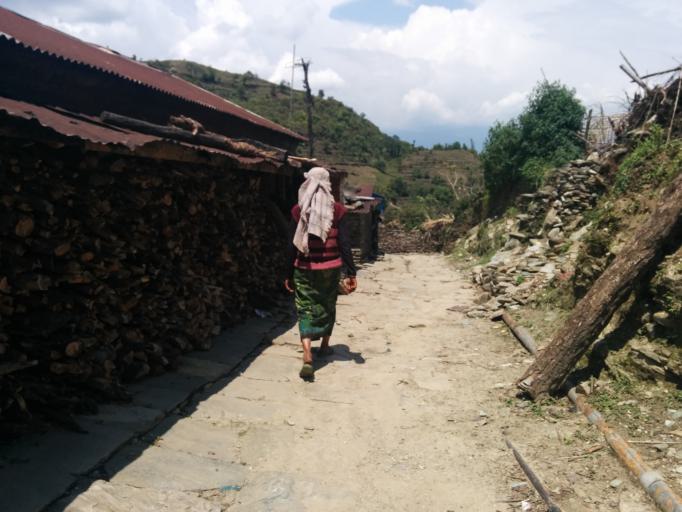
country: NP
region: Western Region
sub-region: Gandaki Zone
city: Pokhara
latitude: 28.2637
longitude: 83.8205
